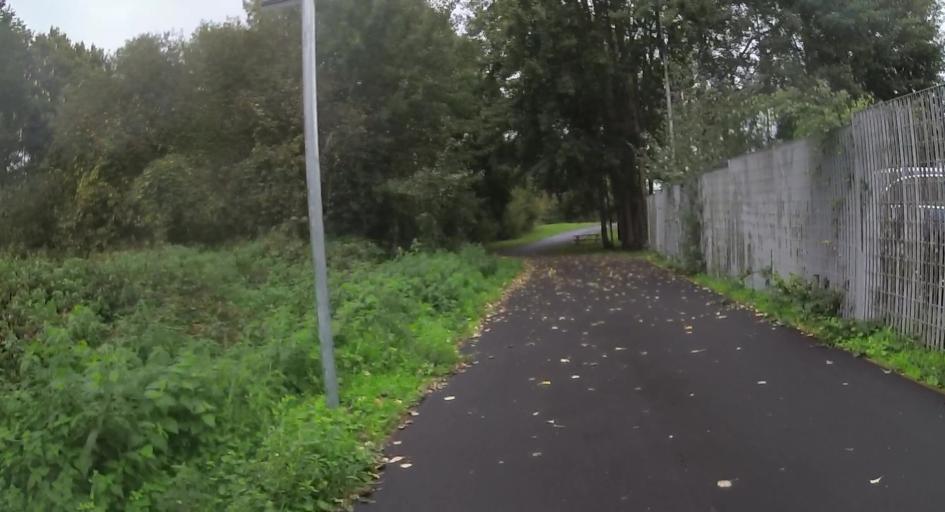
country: GB
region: England
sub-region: Surrey
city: Byfleet
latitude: 51.3560
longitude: -0.4666
